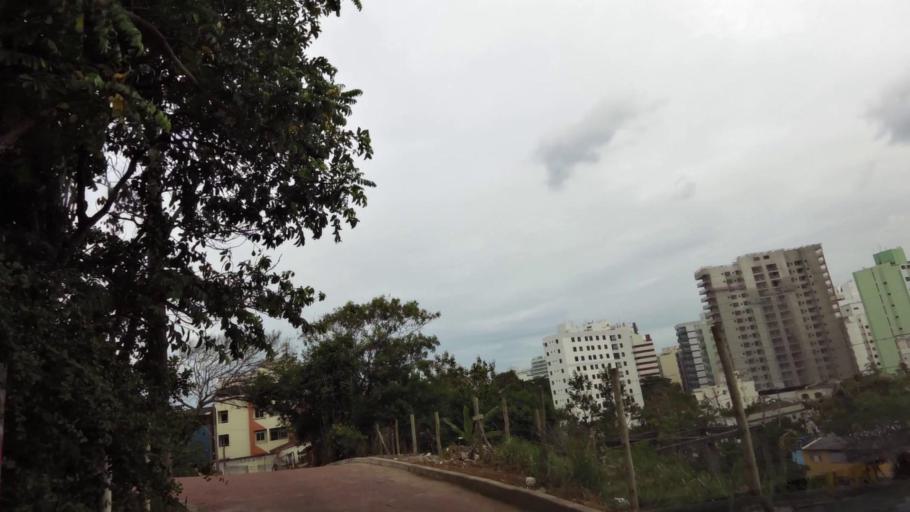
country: BR
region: Espirito Santo
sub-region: Guarapari
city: Guarapari
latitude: -20.6666
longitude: -40.4959
